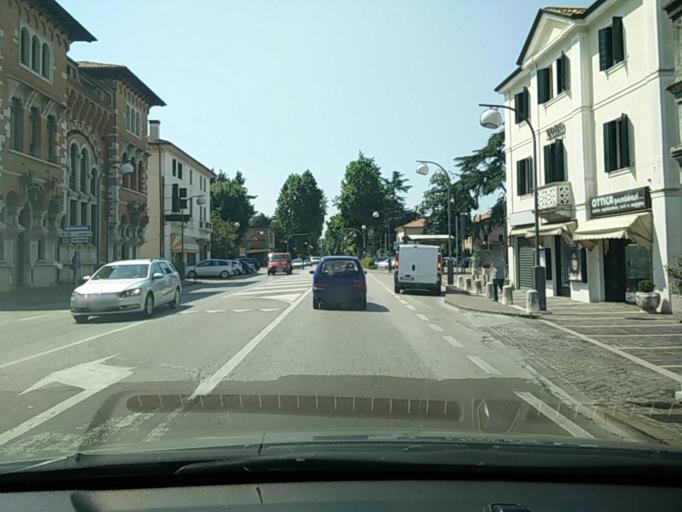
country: IT
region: Veneto
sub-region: Provincia di Treviso
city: Mogliano Veneto
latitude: 45.5608
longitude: 12.2350
